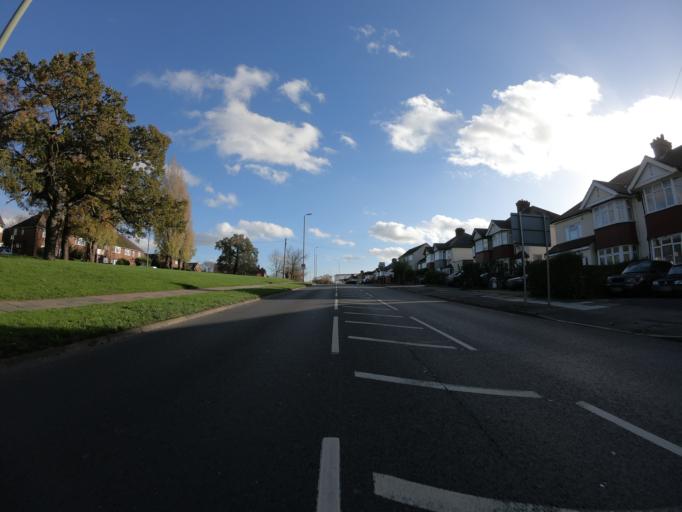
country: GB
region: England
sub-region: Greater London
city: Chislehurst
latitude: 51.4268
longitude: 0.0557
